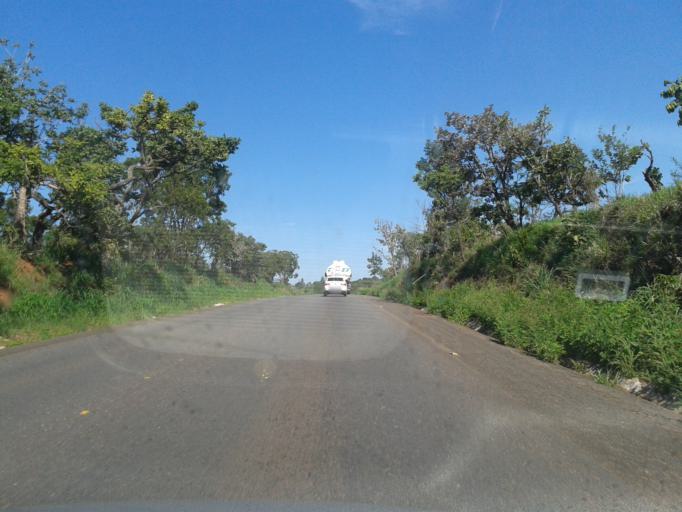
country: BR
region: Goias
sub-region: Bela Vista De Goias
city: Bela Vista de Goias
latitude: -17.0815
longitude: -48.8968
